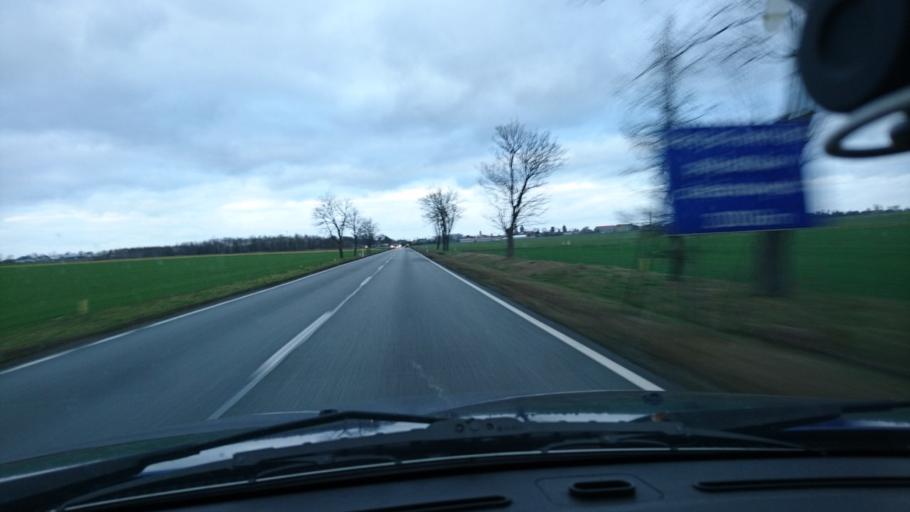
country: PL
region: Opole Voivodeship
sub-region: Powiat kluczborski
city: Byczyna
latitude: 51.1020
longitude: 18.2055
